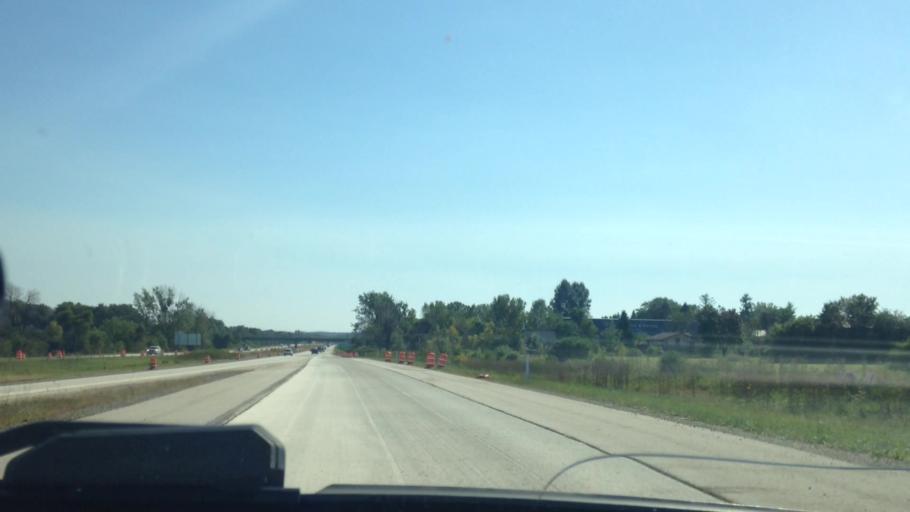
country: US
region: Wisconsin
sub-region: Ozaukee County
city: Grafton
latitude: 43.3358
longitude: -87.9247
